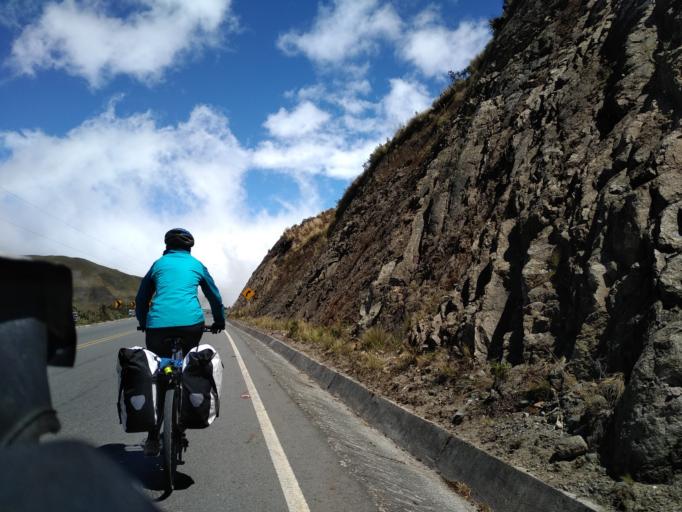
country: EC
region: Cotopaxi
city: Pujili
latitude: -0.9903
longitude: -78.9562
